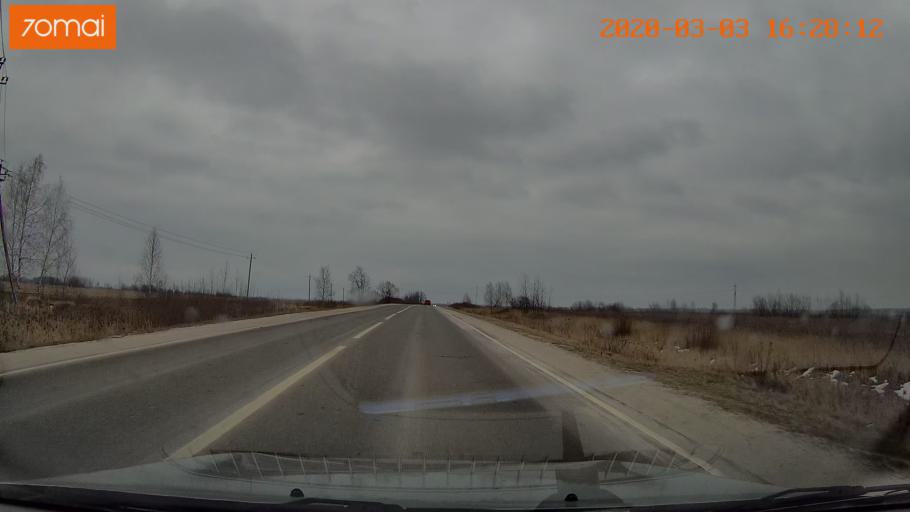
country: RU
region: Moskovskaya
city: Konobeyevo
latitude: 55.4382
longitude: 38.6810
